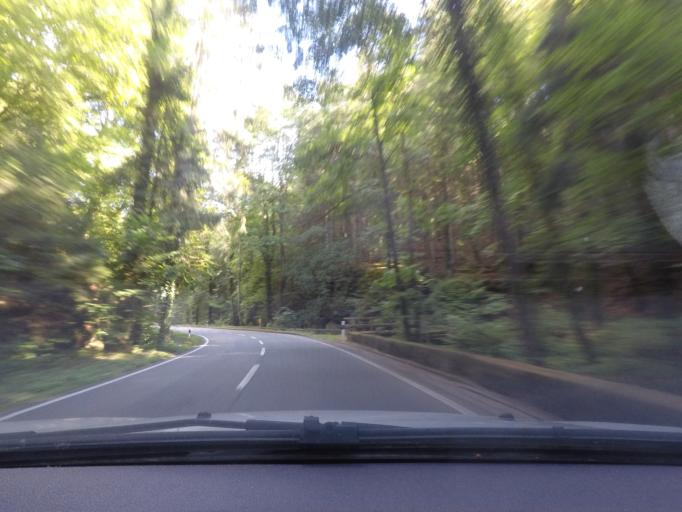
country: LU
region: Luxembourg
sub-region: Canton de Mersch
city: Heffingen
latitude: 49.7528
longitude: 6.2717
